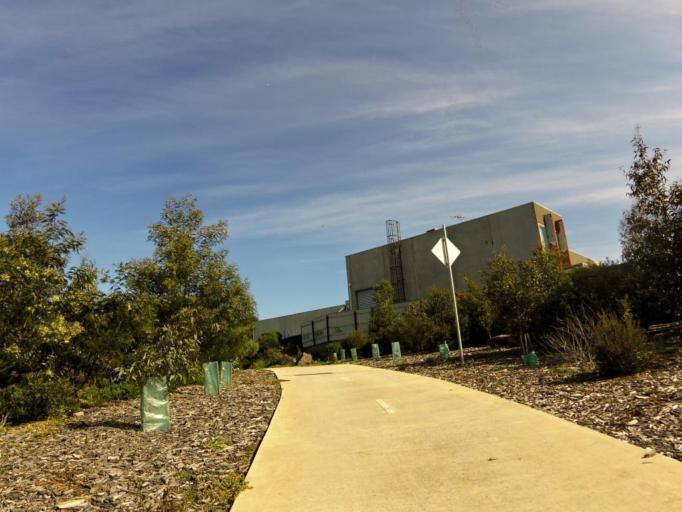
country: AU
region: Victoria
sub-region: Brimbank
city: Brooklyn
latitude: -37.8183
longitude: 144.8244
